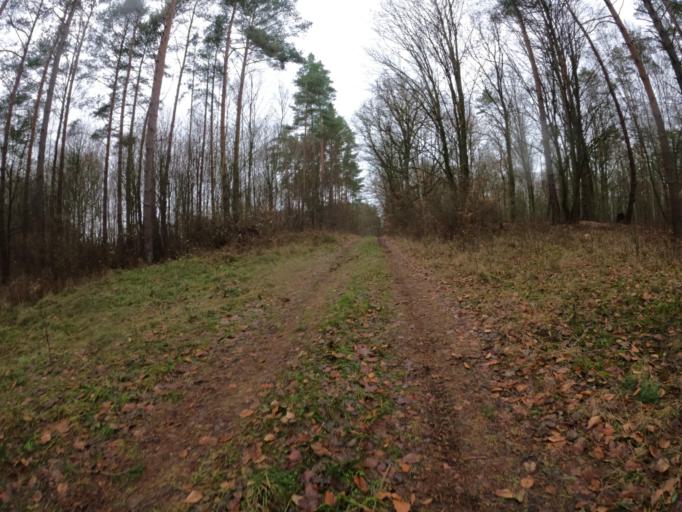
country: PL
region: West Pomeranian Voivodeship
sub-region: Powiat mysliborski
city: Debno
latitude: 52.7496
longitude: 14.7762
